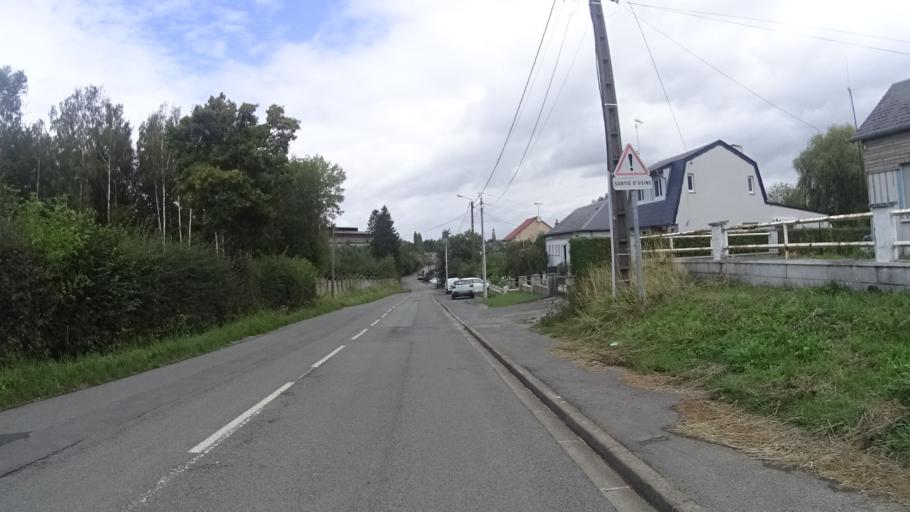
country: FR
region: Nord-Pas-de-Calais
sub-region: Departement du Nord
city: Berlaimont
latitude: 50.1932
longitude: 3.8077
